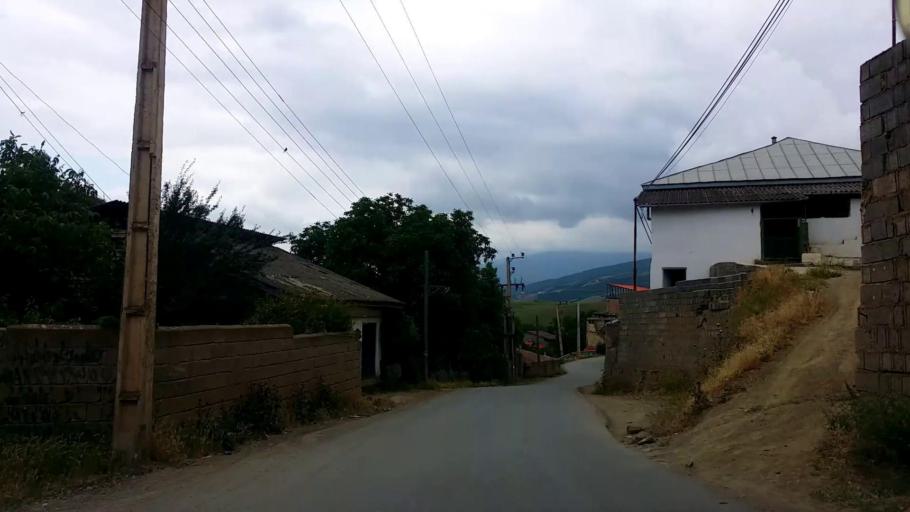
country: IR
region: Mazandaran
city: Chalus
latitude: 36.5158
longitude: 51.2592
